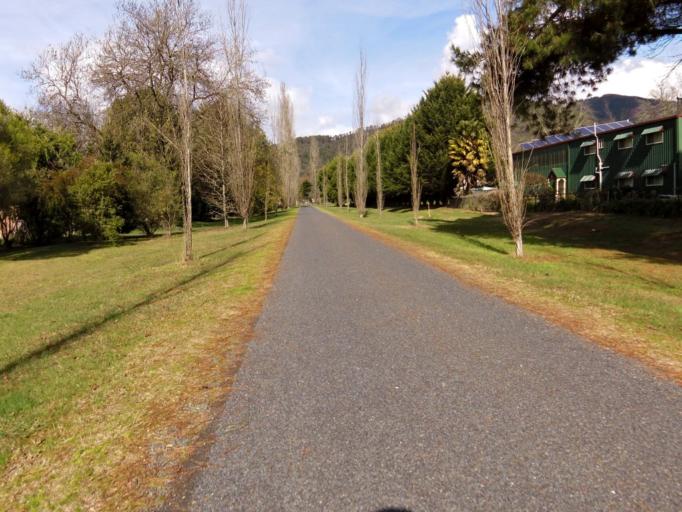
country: AU
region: Victoria
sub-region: Alpine
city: Mount Beauty
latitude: -36.7217
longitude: 146.9456
